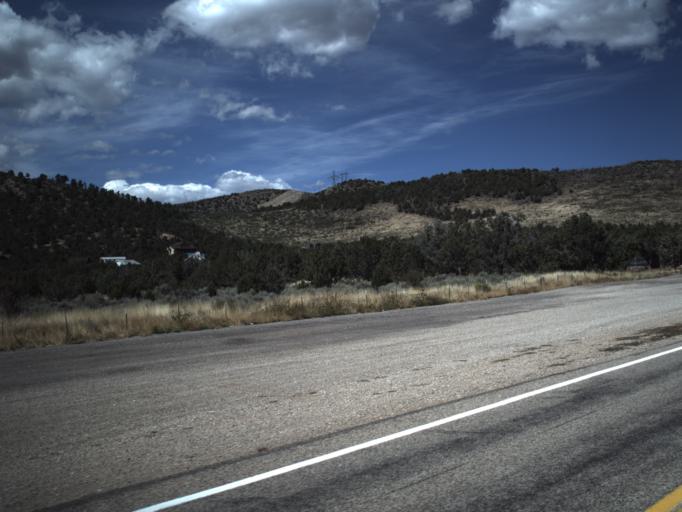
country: US
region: Utah
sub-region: Washington County
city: Enterprise
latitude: 37.4195
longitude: -113.6316
